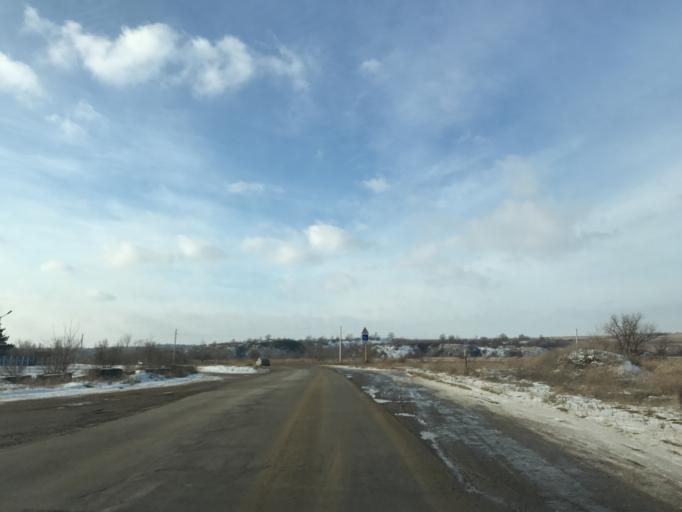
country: RU
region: Rostov
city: Staraya Stanitsa
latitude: 48.2409
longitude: 40.4106
